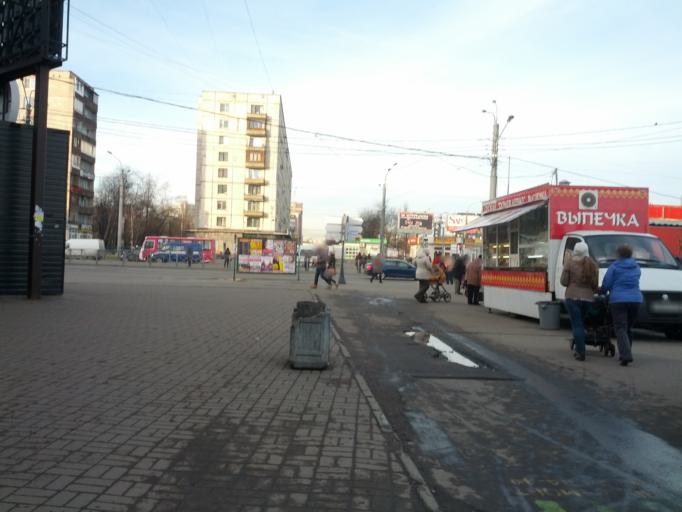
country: RU
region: St.-Petersburg
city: Krasnogvargeisky
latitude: 59.9060
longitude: 30.4825
